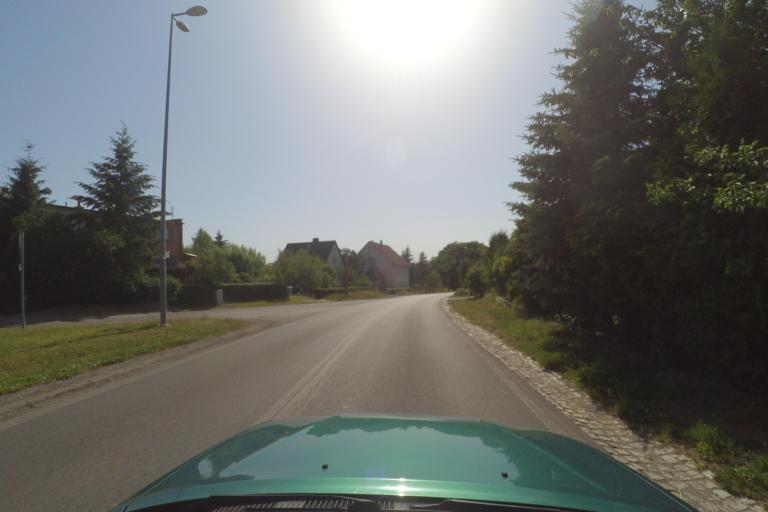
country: PL
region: Lower Silesian Voivodeship
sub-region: Powiat lubanski
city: Luban
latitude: 51.1206
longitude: 15.3225
